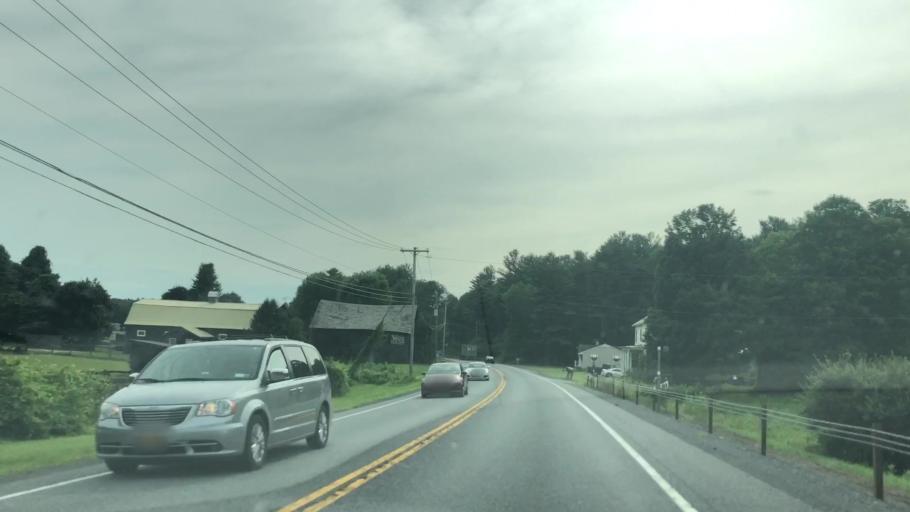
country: US
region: New York
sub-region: Warren County
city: Queensbury
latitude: 43.4043
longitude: -73.5999
